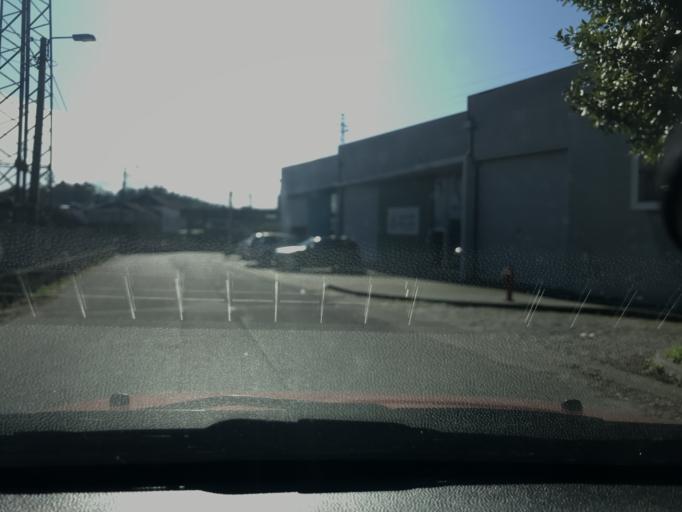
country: PT
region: Braga
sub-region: Vila Nova de Famalicao
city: Vila Nova de Famalicao
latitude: 41.4174
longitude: -8.5052
